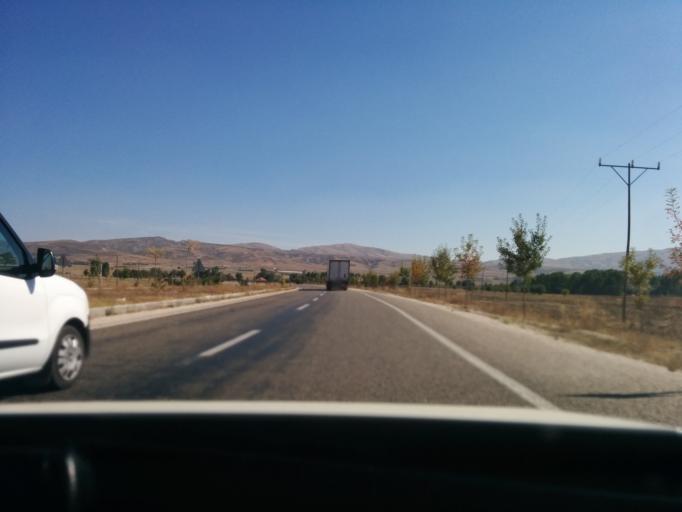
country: TR
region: Antalya
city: Kizilcadag
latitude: 37.0080
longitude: 29.9266
